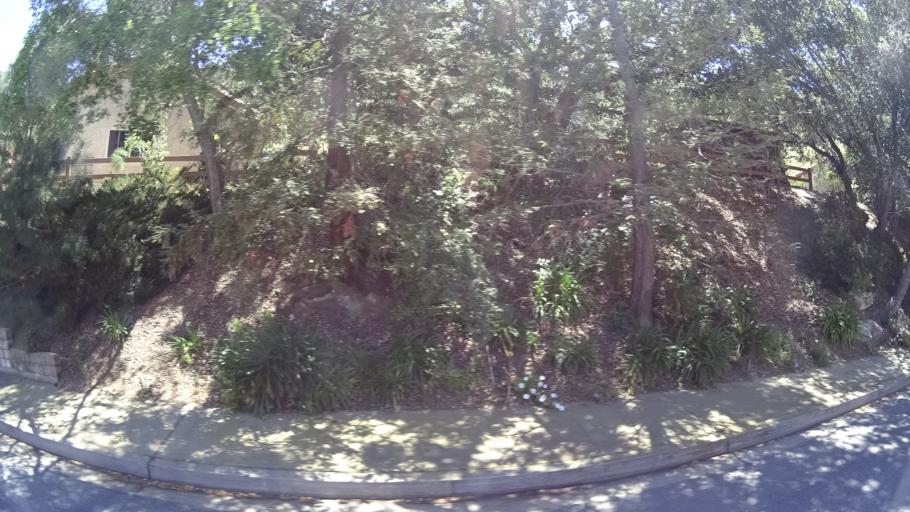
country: US
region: California
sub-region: Ventura County
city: Casa Conejo
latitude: 34.1745
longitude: -118.8922
